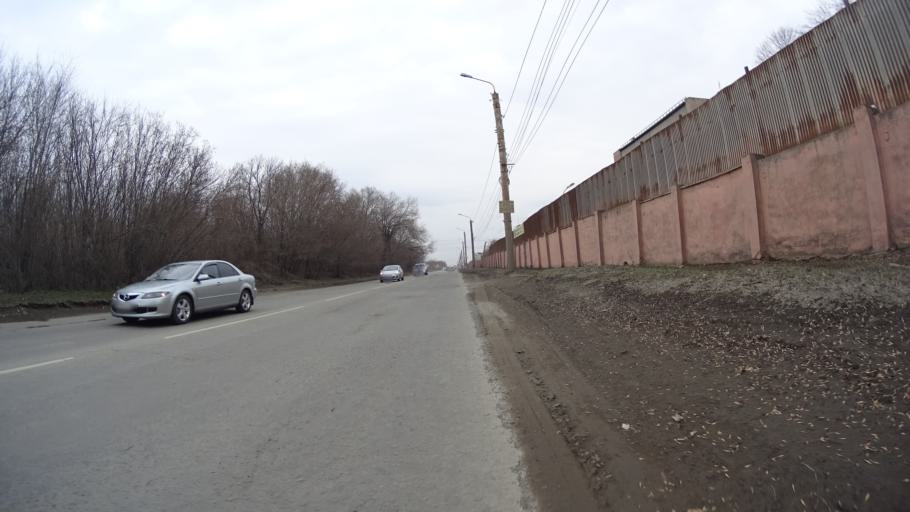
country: RU
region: Chelyabinsk
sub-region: Gorod Chelyabinsk
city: Chelyabinsk
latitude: 55.1587
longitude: 61.4727
